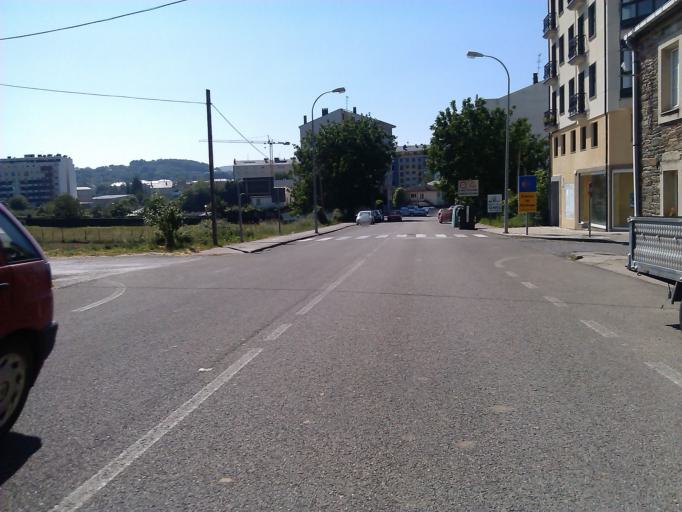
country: ES
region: Galicia
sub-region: Provincia de Lugo
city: Sarria
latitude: 42.7739
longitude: -7.4027
